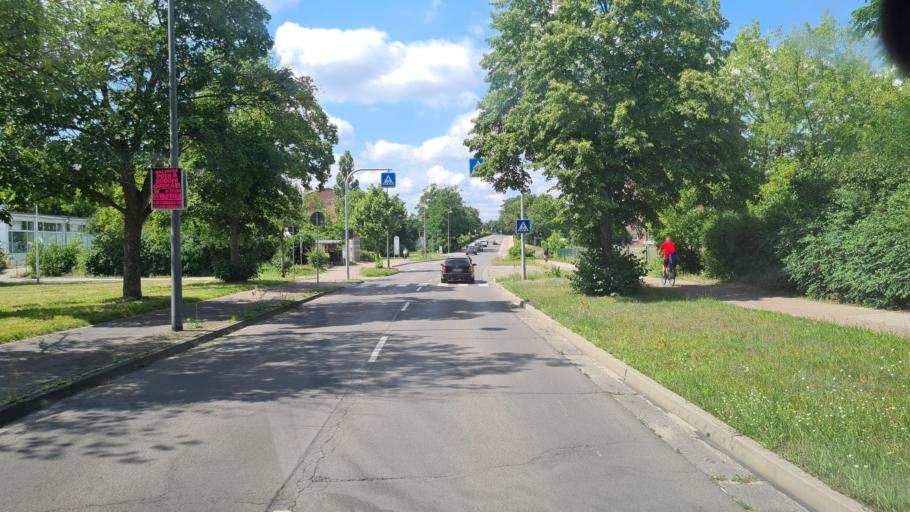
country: DE
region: Brandenburg
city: Senftenberg
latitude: 51.5149
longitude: 13.9844
